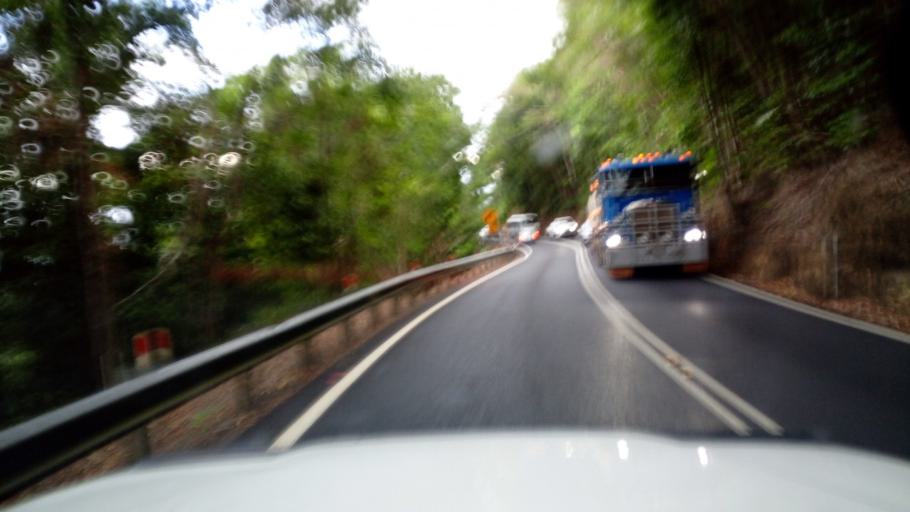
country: AU
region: Queensland
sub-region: Tablelands
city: Kuranda
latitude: -16.8354
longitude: 145.6714
